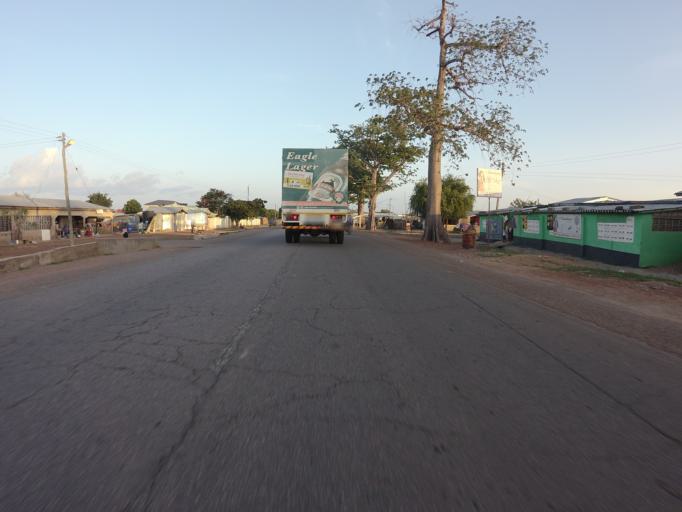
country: GH
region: Upper East
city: Navrongo
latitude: 10.9648
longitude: -1.1006
